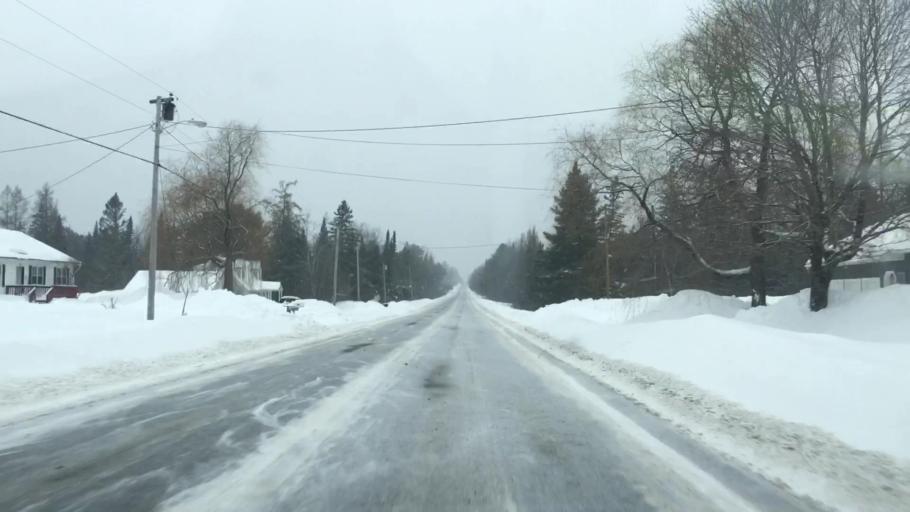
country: US
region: Maine
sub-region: Penobscot County
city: Medway
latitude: 45.5258
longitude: -68.3574
